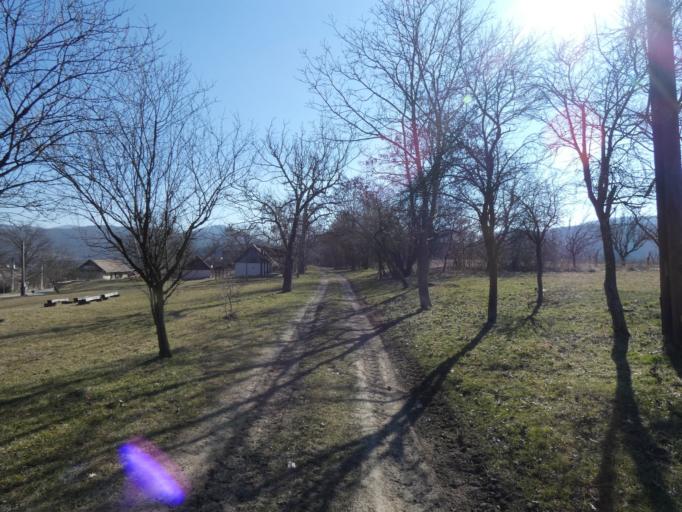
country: HU
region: Pest
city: Szob
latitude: 47.9358
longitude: 18.8188
